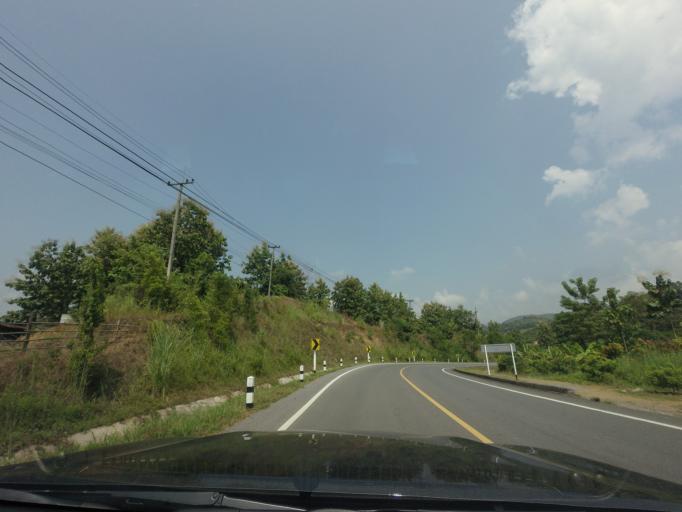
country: TH
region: Nan
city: Santi Suk
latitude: 18.8969
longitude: 100.8389
